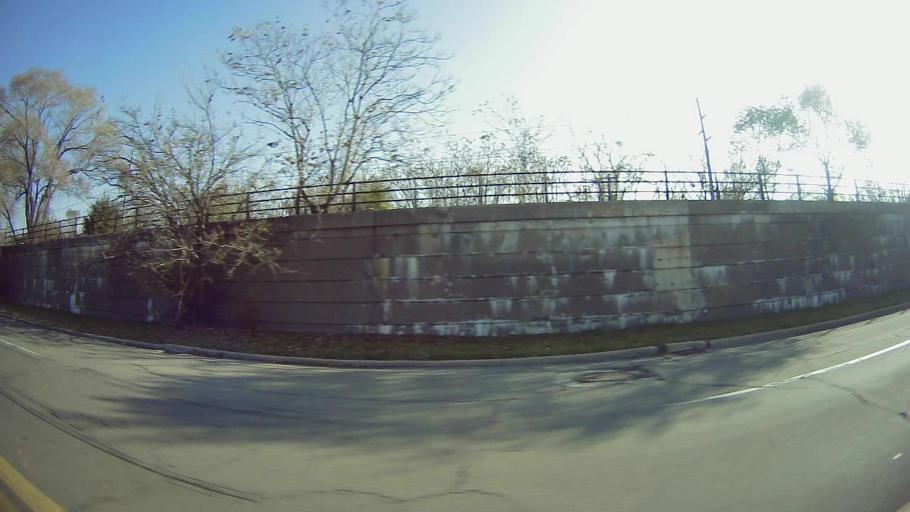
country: US
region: Michigan
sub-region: Wayne County
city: Dearborn
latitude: 42.3281
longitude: -83.1664
